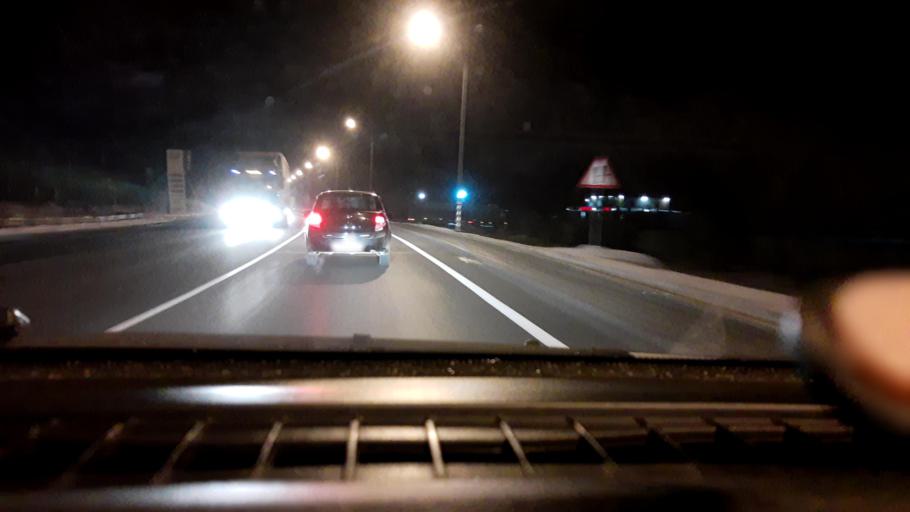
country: RU
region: Nizjnij Novgorod
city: Spasskoye
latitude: 56.0497
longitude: 45.5593
